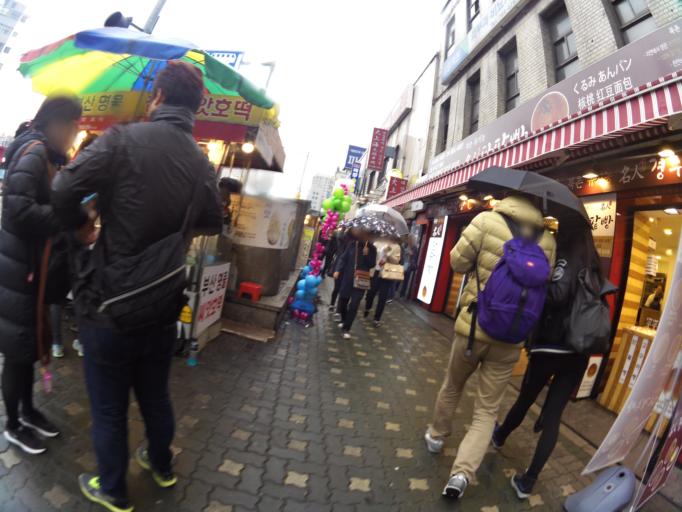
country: KR
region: Seoul
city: Seoul
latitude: 37.5716
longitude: 127.0110
